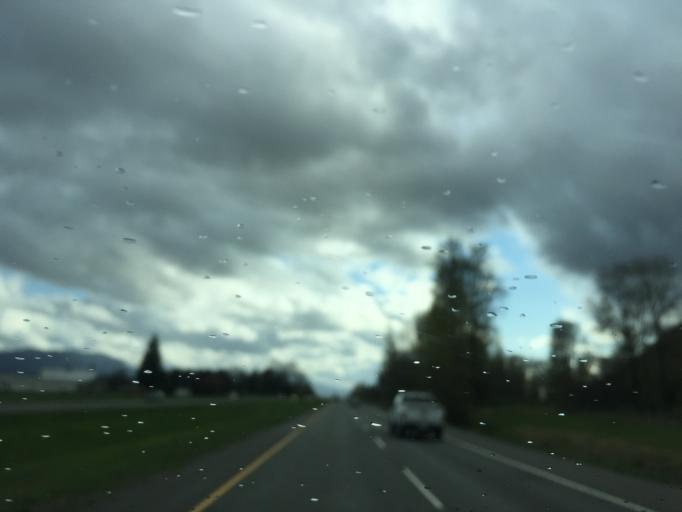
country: CA
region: British Columbia
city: Abbotsford
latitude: 49.1122
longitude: -122.1077
